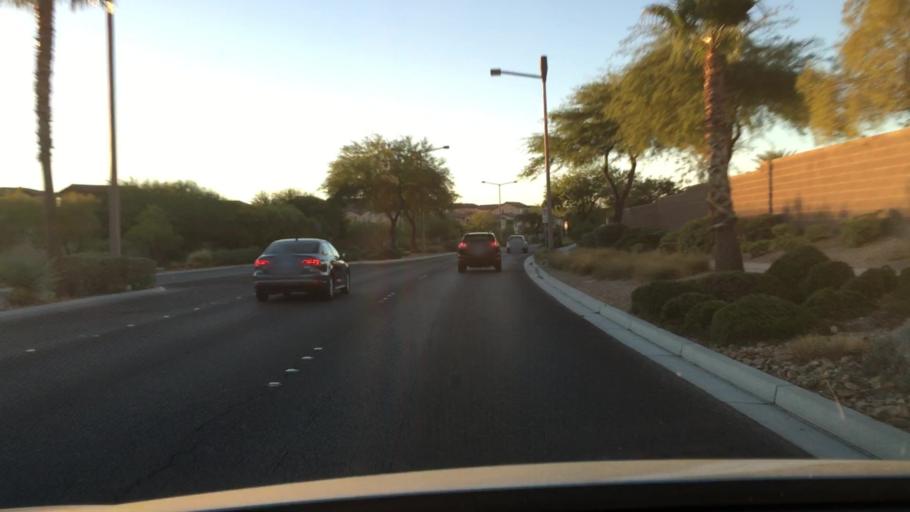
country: US
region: Nevada
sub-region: Clark County
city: Summerlin South
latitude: 36.1536
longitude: -115.3444
